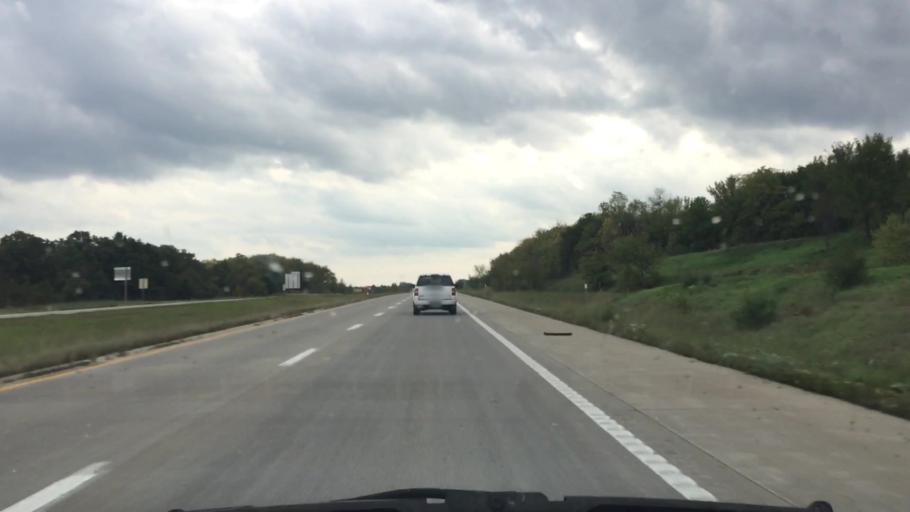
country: US
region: Missouri
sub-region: Clinton County
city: Cameron
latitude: 39.6666
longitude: -94.2362
